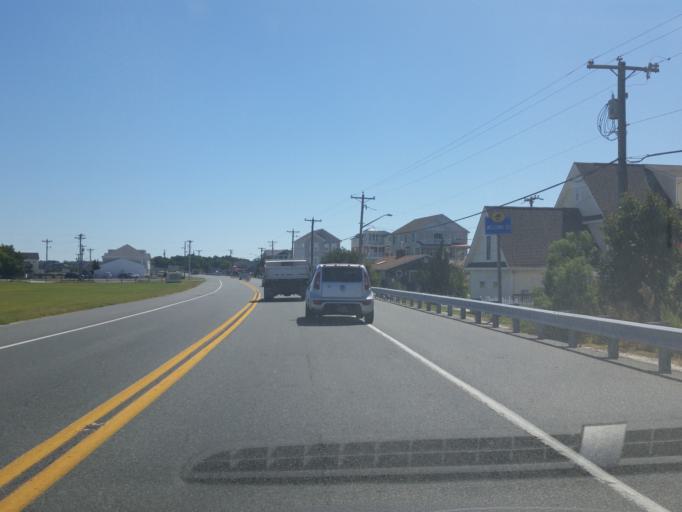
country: US
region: Delaware
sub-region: Sussex County
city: Bethany Beach
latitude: 38.4542
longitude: -75.0682
